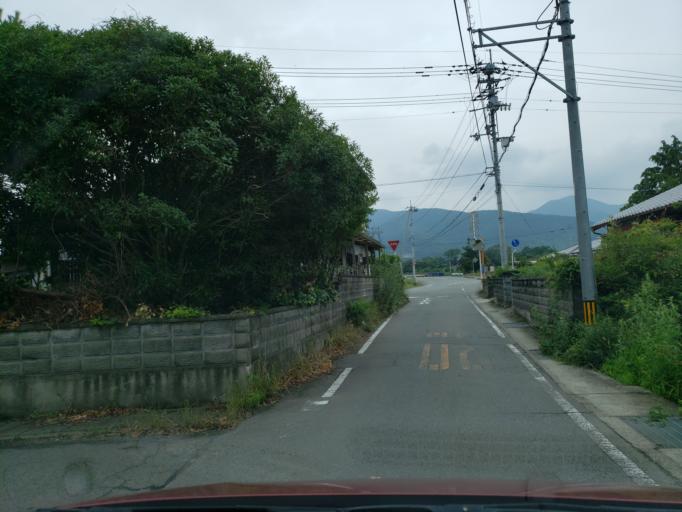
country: JP
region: Tokushima
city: Kamojimacho-jogejima
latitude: 34.1016
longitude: 134.2782
